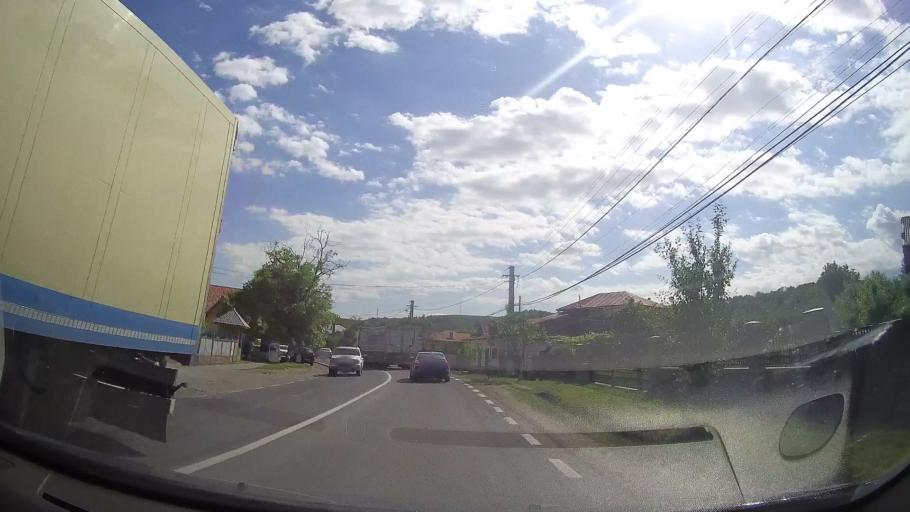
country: RO
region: Prahova
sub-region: Comuna Izvoarele
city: Homoraciu
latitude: 45.2668
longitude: 26.0146
